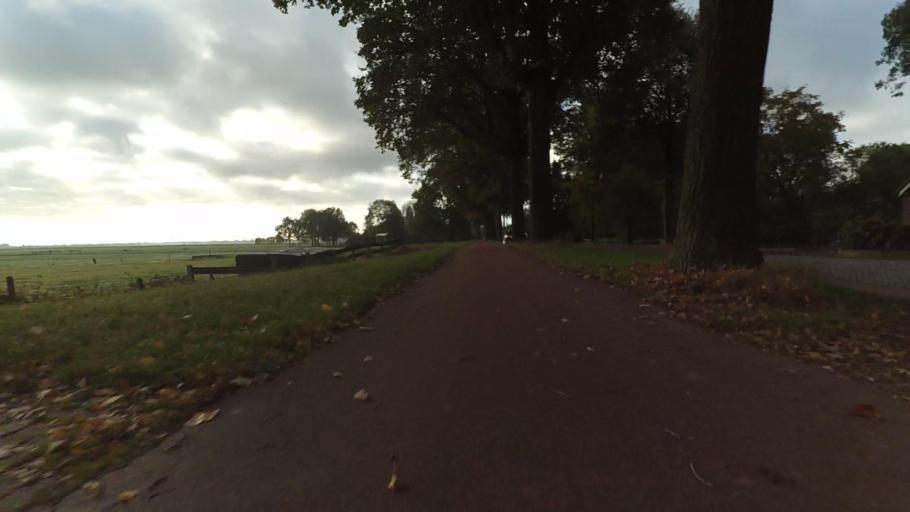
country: NL
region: North Holland
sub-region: Gemeente Blaricum
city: Blaricum
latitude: 52.2543
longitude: 5.2679
